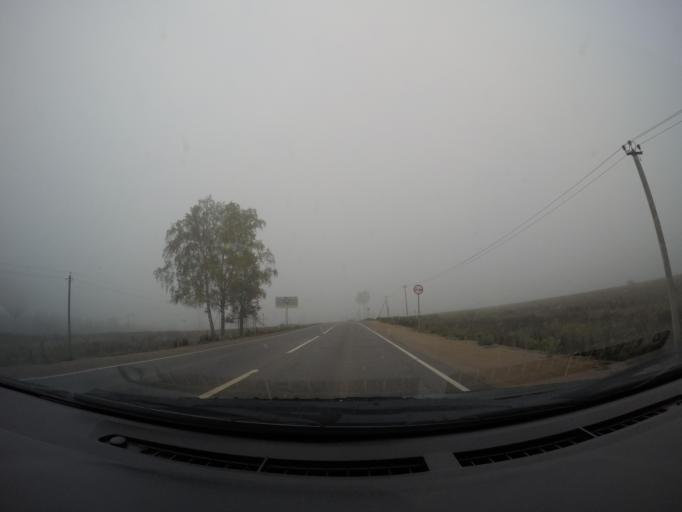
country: RU
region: Moskovskaya
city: Ruza
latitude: 55.7291
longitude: 36.3354
